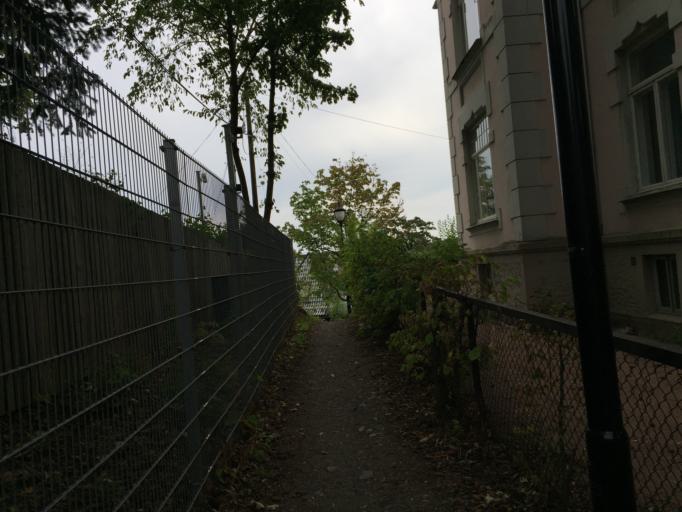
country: NO
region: Oslo
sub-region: Oslo
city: Sjolyststranda
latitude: 59.9151
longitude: 10.7037
